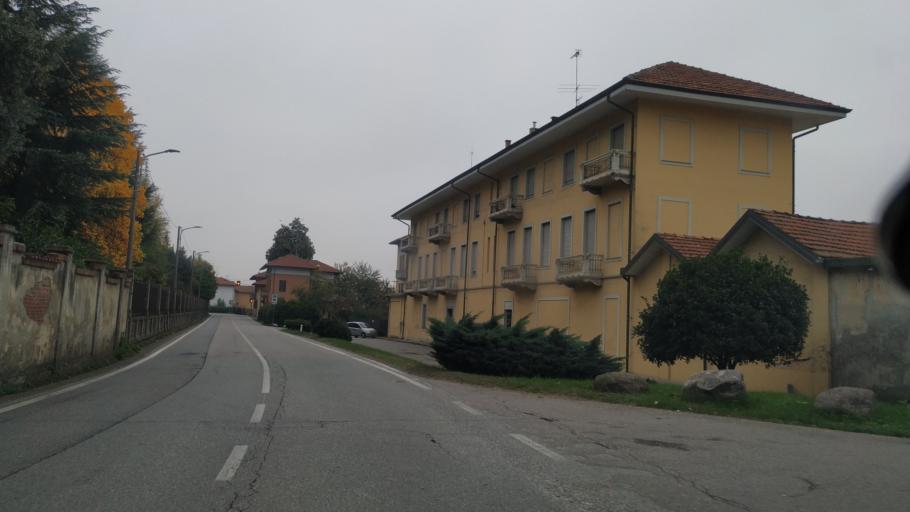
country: IT
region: Piedmont
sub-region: Provincia di Biella
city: Cossato
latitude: 45.5725
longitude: 8.1858
